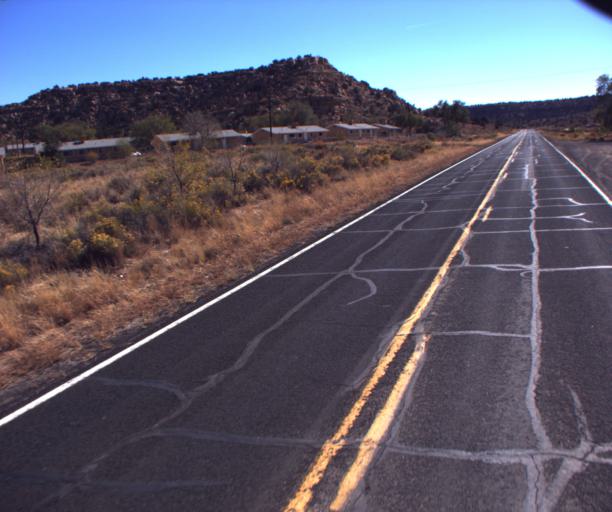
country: US
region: Arizona
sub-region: Navajo County
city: First Mesa
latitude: 35.8245
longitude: -110.2202
